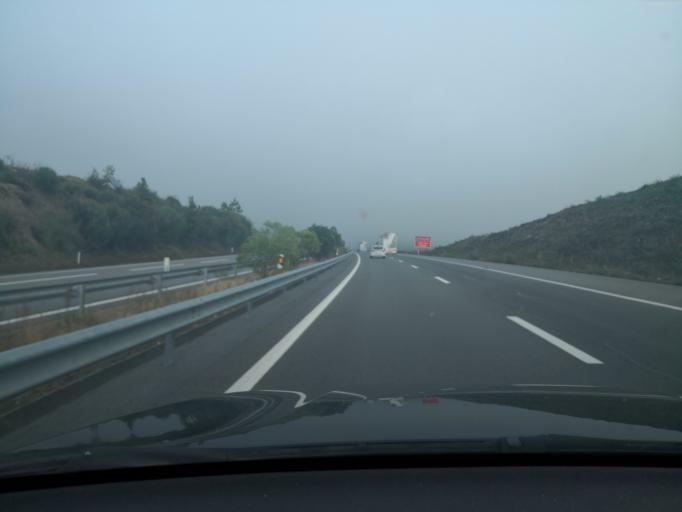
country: PT
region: Braga
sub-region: Fafe
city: Fafe
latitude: 41.4443
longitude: -8.0802
